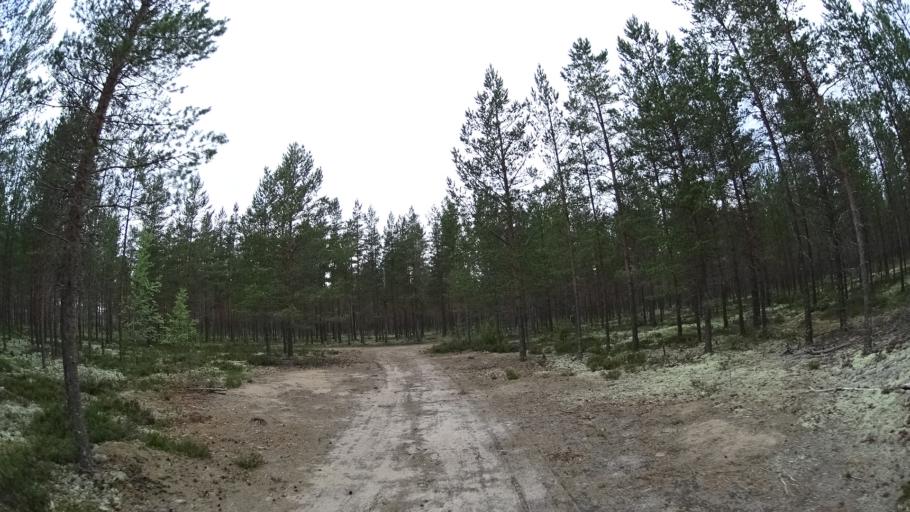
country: FI
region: Satakunta
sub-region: Pohjois-Satakunta
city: Jaemijaervi
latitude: 61.7619
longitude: 22.7859
